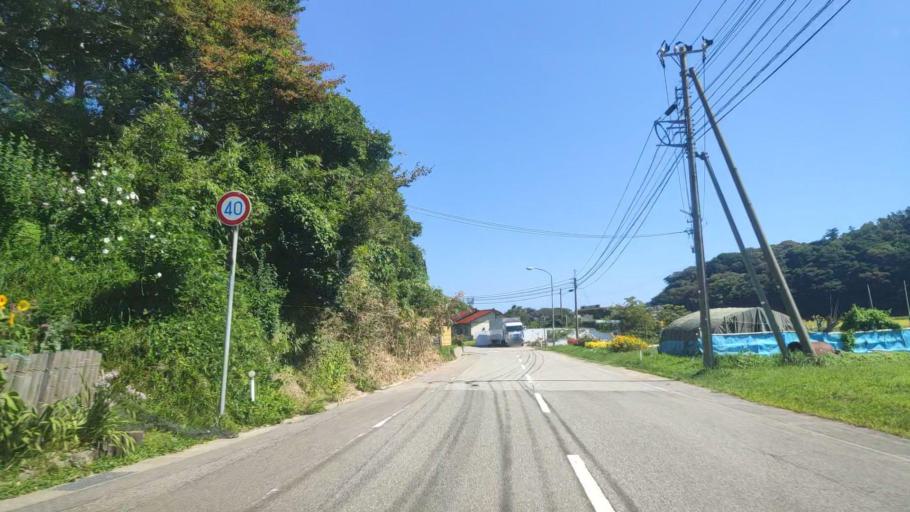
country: JP
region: Ishikawa
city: Nanao
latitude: 37.5257
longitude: 137.3205
